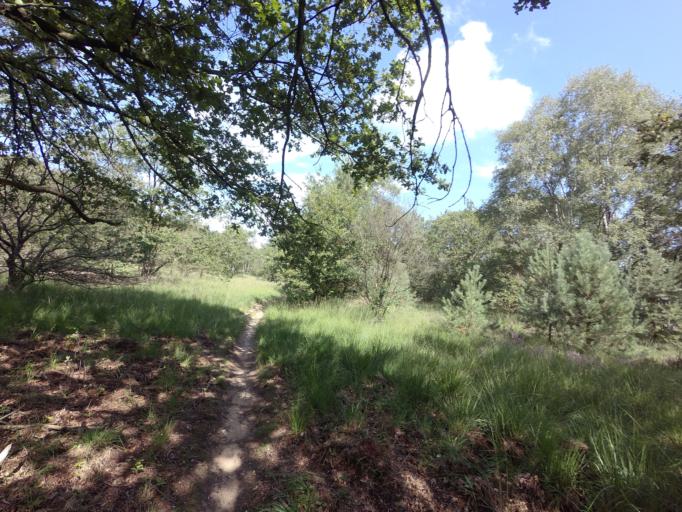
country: NL
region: Gelderland
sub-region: Gemeente Ede
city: Ede
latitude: 52.0534
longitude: 5.6973
